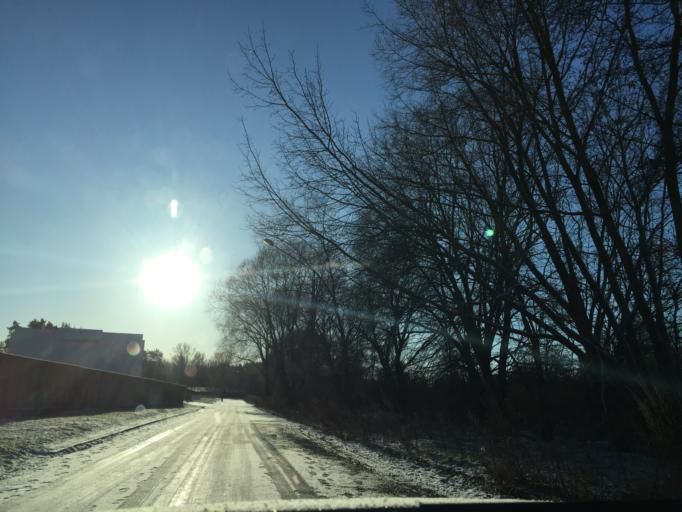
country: LV
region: Kekava
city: Balozi
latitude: 56.9100
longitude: 24.1396
